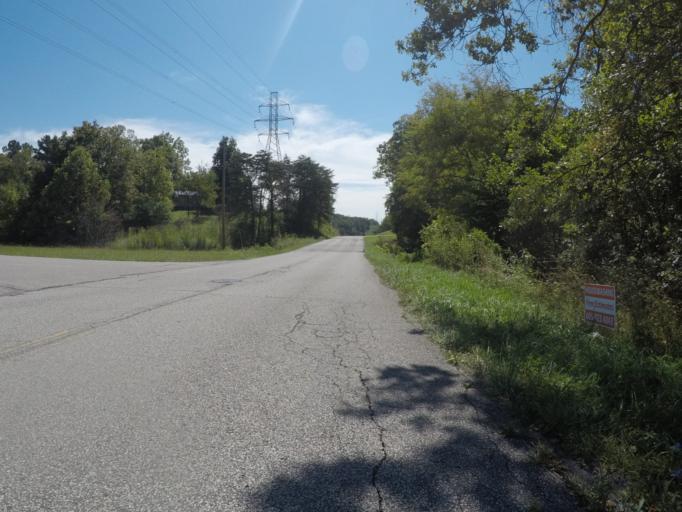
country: US
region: Kentucky
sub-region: Boyd County
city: Catlettsburg
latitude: 38.4052
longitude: -82.6517
